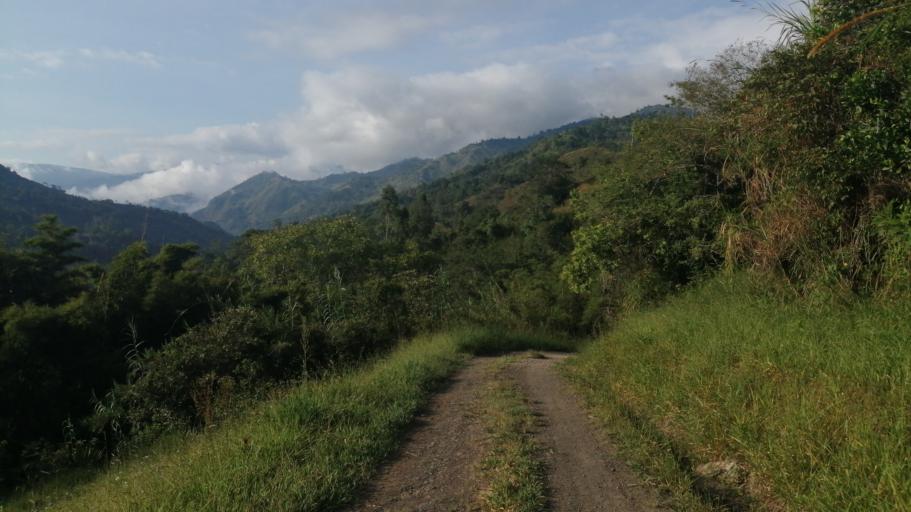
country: CO
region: Boyaca
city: Garagoa
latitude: 5.0731
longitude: -73.3892
